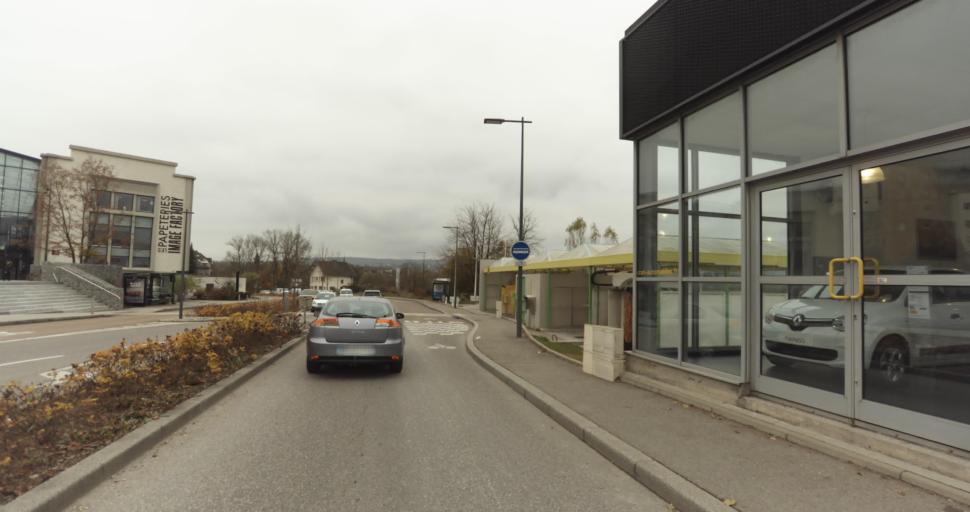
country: FR
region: Rhone-Alpes
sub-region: Departement de la Haute-Savoie
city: Cran-Gevrier
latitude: 45.9081
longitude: 6.1037
